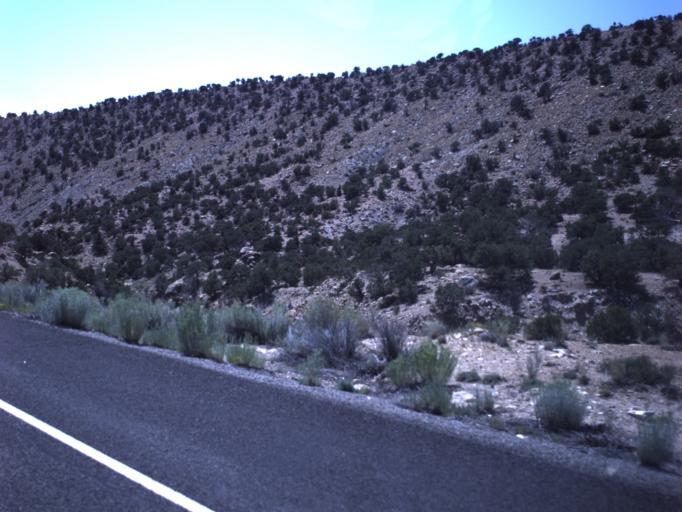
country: US
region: Utah
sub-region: Emery County
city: Orangeville
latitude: 39.2845
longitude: -111.1058
